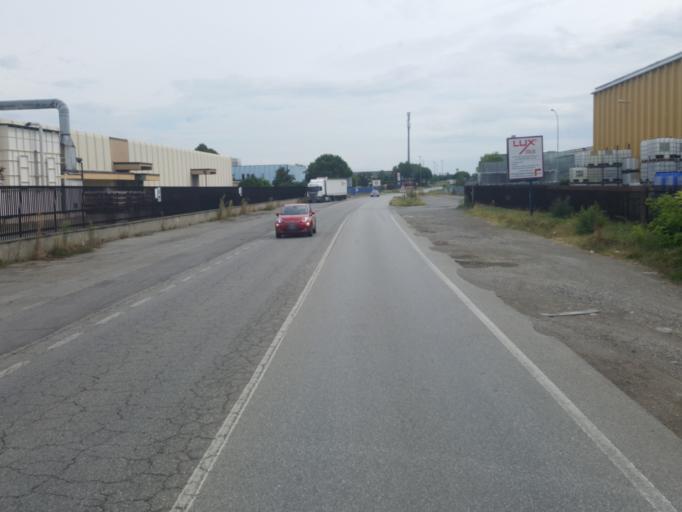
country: IT
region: Lombardy
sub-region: Citta metropolitana di Milano
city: Cambiago
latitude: 45.5806
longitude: 9.4368
